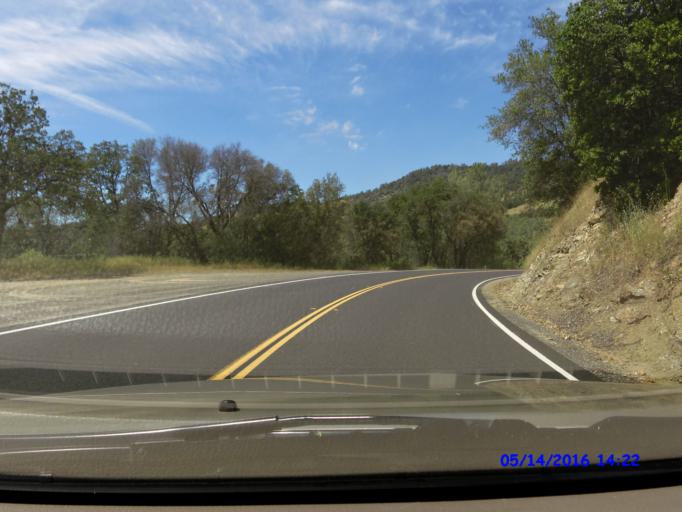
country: US
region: California
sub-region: Tuolumne County
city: Tuolumne City
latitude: 37.6862
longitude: -120.1774
